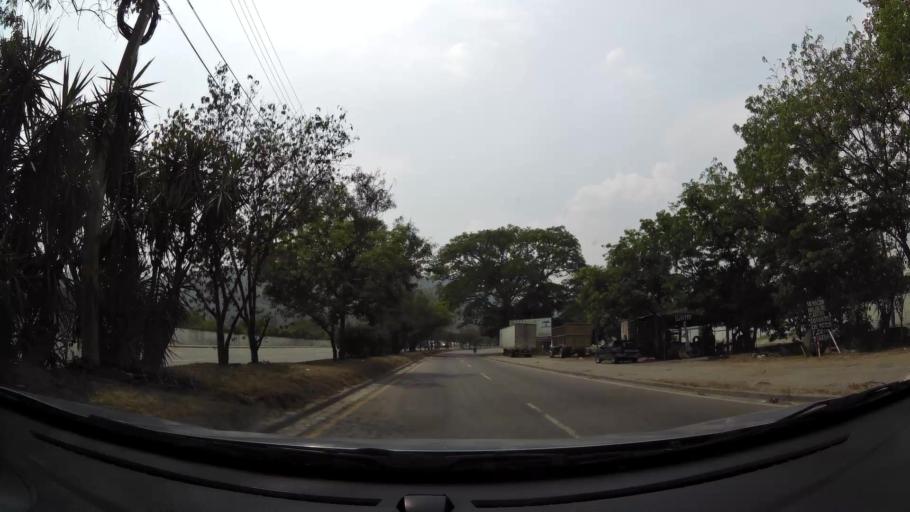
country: HN
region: Cortes
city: Nuevo Chamelecon
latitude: 15.4086
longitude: -88.0109
